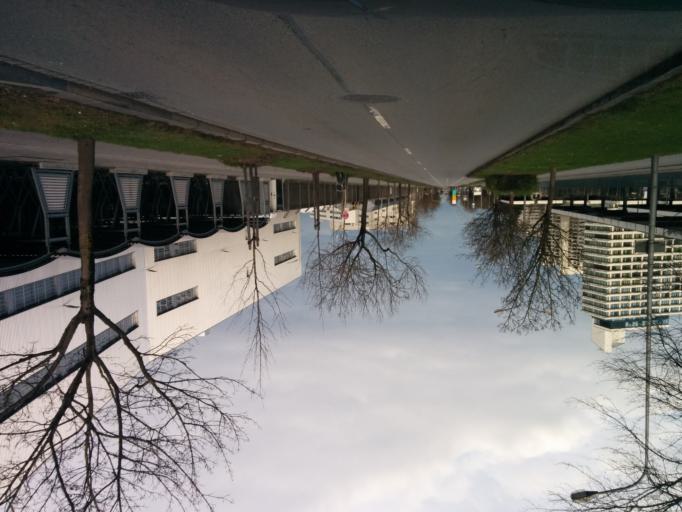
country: DE
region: Bavaria
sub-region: Upper Bavaria
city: Munich
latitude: 48.1788
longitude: 11.5567
